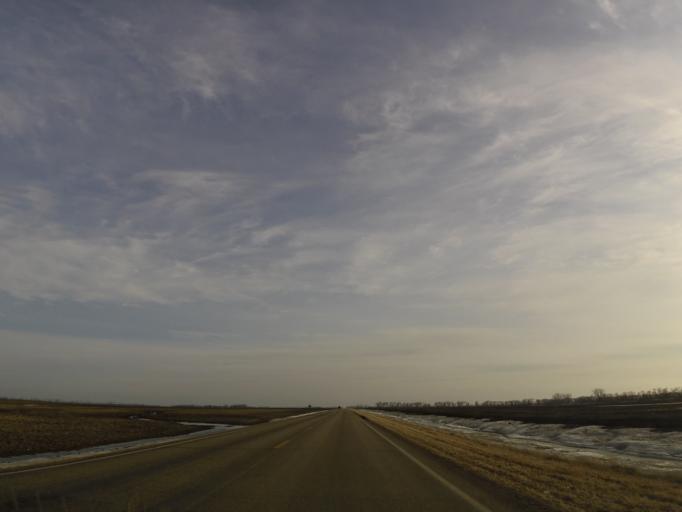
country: US
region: North Dakota
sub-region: Walsh County
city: Grafton
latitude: 48.4245
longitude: -97.2996
